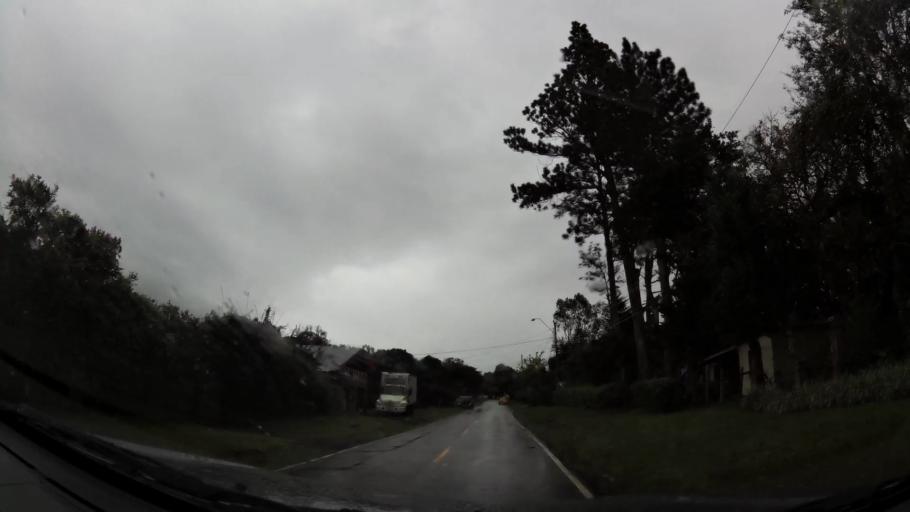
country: PA
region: Chiriqui
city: Volcan
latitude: 8.7903
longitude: -82.6518
